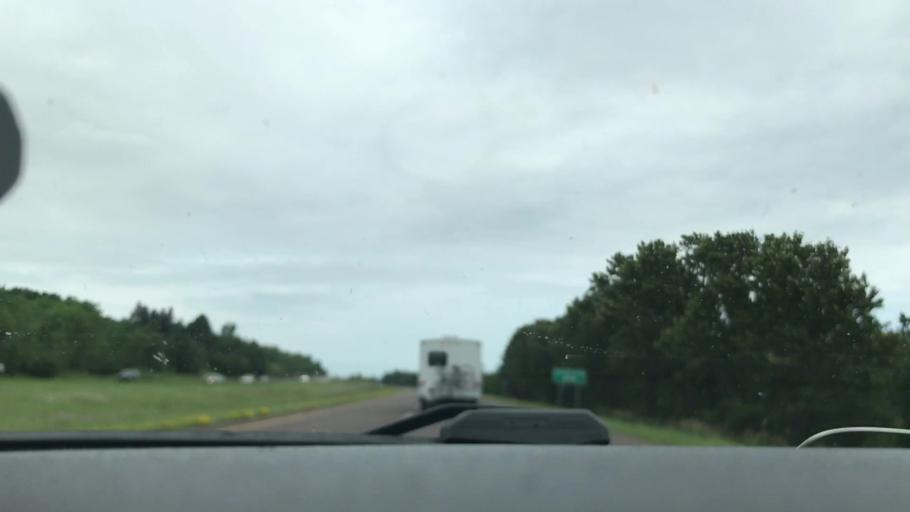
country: US
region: Minnesota
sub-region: Lake County
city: Two Harbors
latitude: 46.9791
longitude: -91.7485
